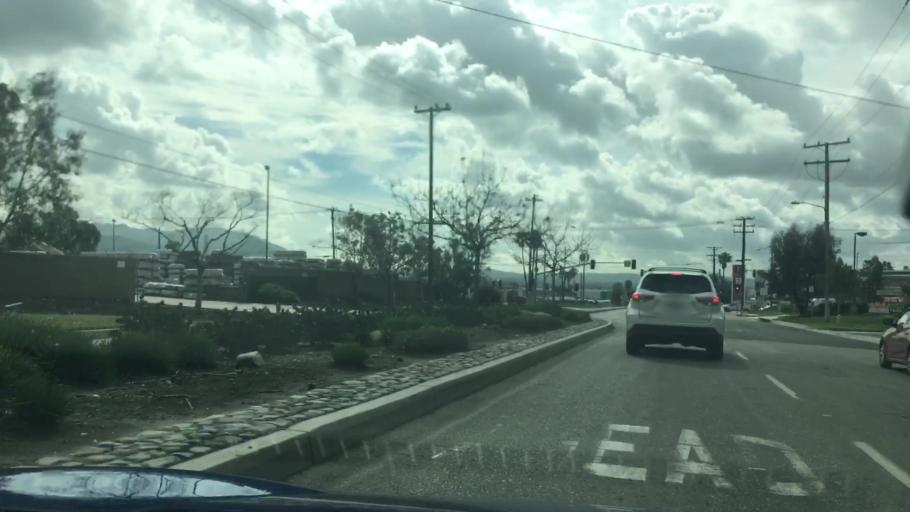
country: US
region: California
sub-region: Riverside County
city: Highgrove
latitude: 34.0396
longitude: -117.3676
